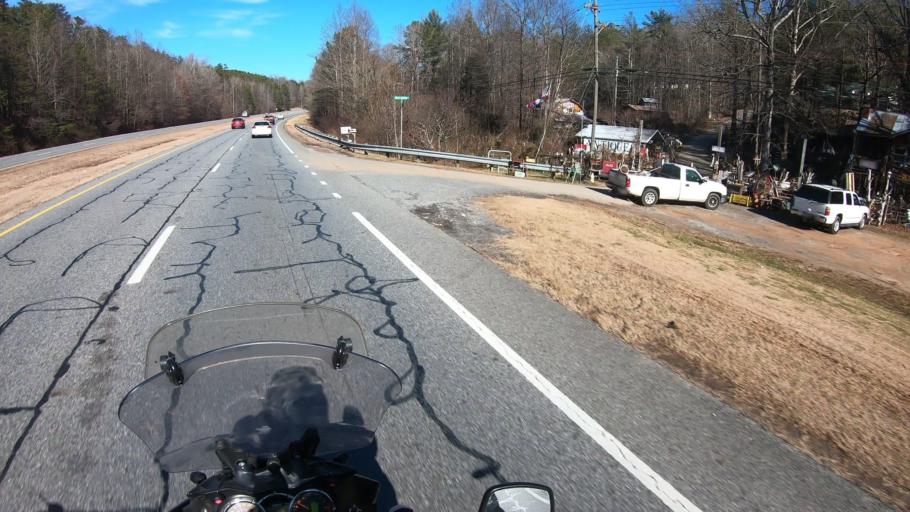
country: US
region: Georgia
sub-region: Gilmer County
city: Ellijay
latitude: 34.7660
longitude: -84.3996
